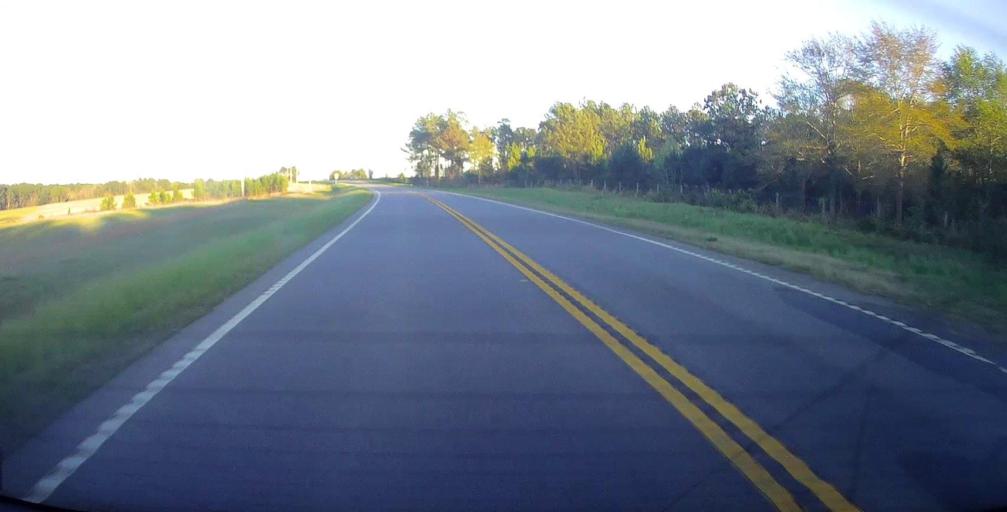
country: US
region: Georgia
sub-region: Crisp County
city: Cordele
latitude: 31.9508
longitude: -83.7151
